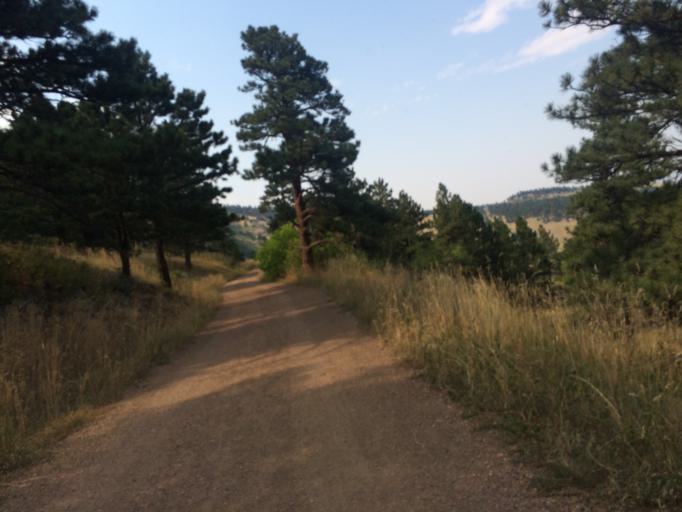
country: US
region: Colorado
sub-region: Boulder County
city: Boulder
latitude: 39.9298
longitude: -105.2742
